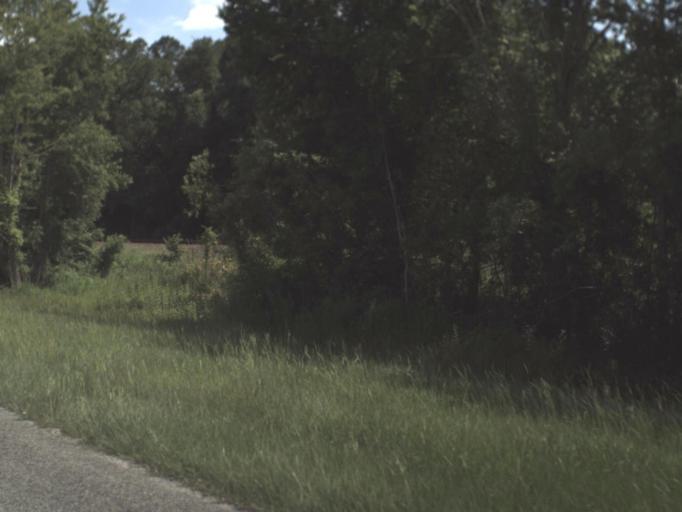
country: US
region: Florida
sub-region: Alachua County
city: Waldo
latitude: 29.7033
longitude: -82.1342
